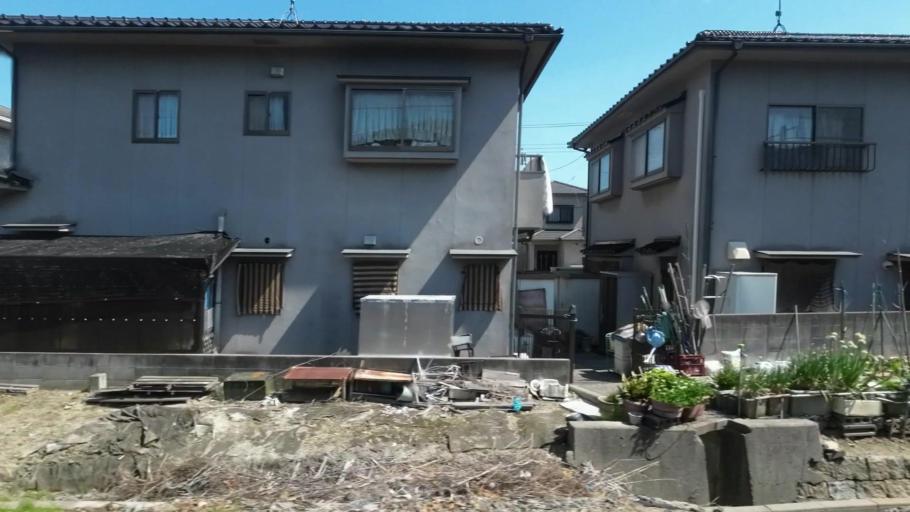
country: JP
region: Hiroshima
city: Fukuyama
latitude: 34.4684
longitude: 133.2990
